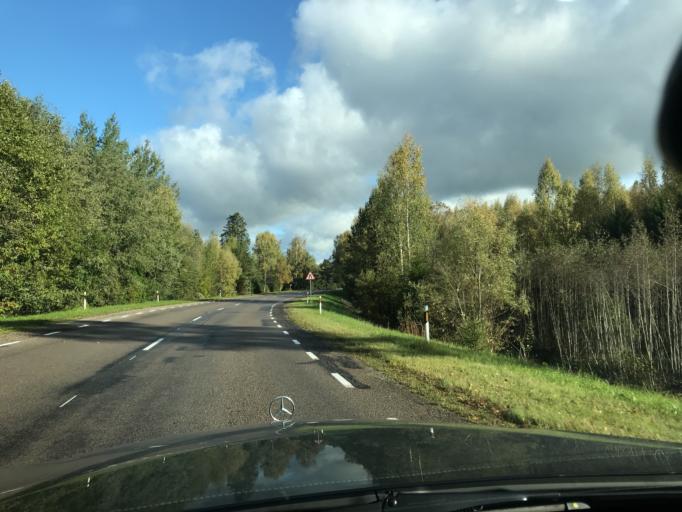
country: EE
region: Valgamaa
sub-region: Torva linn
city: Torva
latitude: 58.0025
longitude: 26.0804
